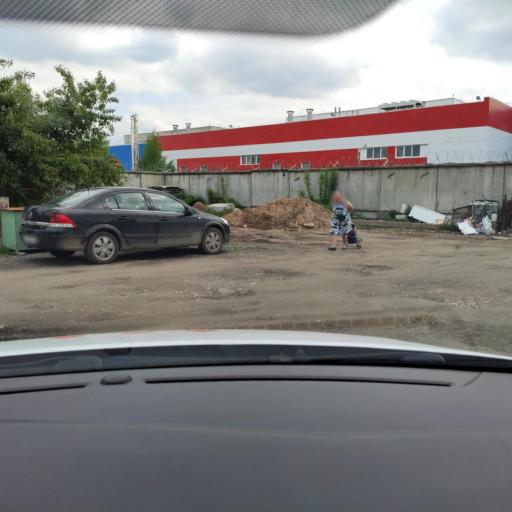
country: RU
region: Tatarstan
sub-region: Gorod Kazan'
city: Kazan
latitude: 55.8687
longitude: 49.1099
